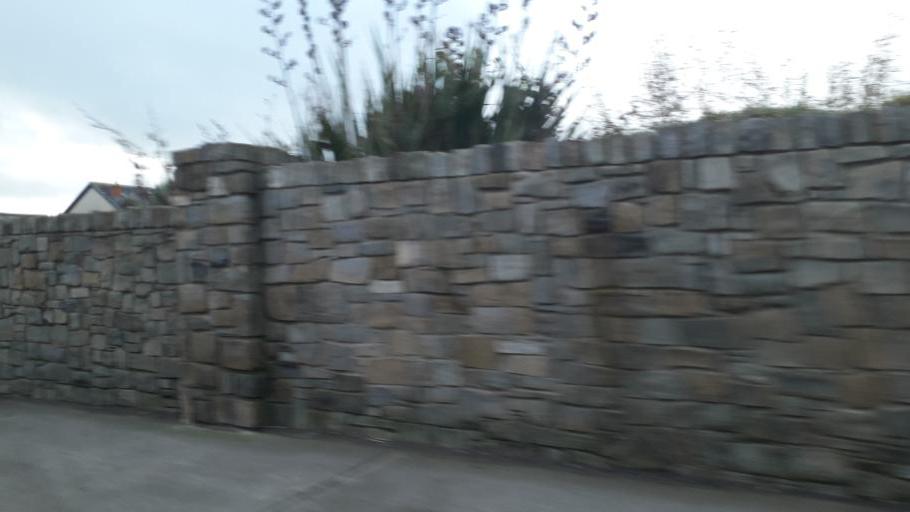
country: IE
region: Leinster
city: An Ros
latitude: 53.5275
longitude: -6.0912
